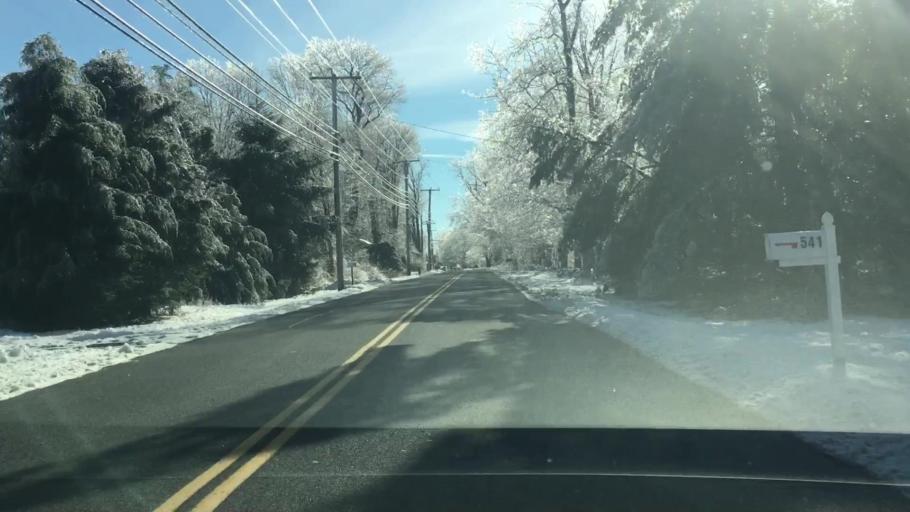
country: US
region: Connecticut
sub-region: Fairfield County
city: Trumbull
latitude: 41.3320
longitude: -73.2227
